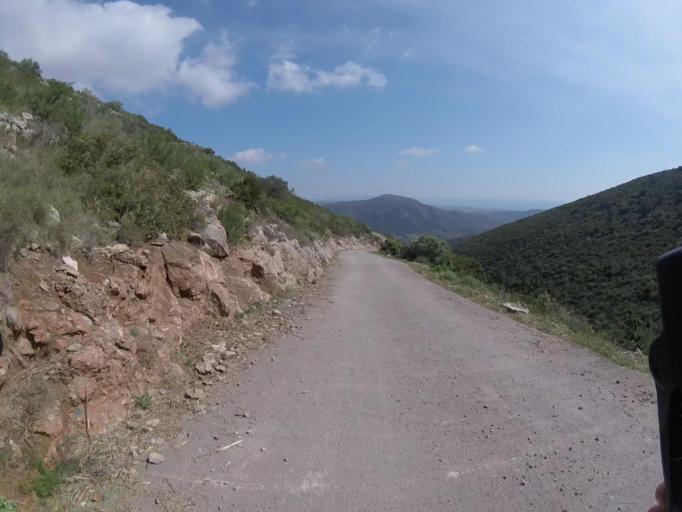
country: ES
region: Valencia
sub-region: Provincia de Castello
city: Benicassim
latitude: 40.0973
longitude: 0.0451
